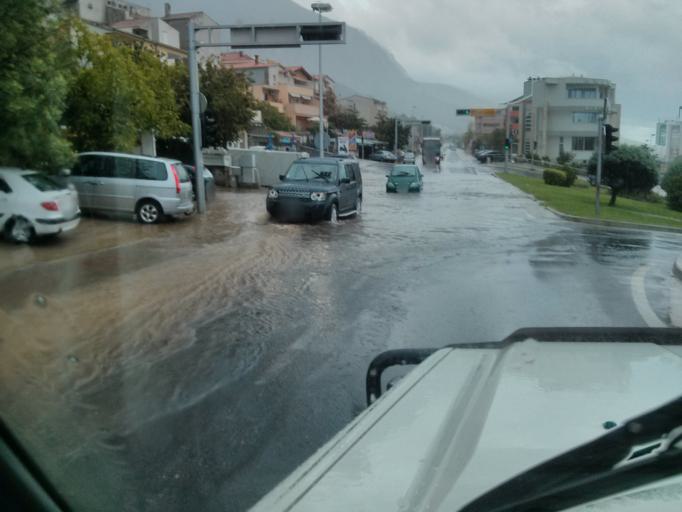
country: HR
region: Splitsko-Dalmatinska
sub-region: Grad Makarska
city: Makarska
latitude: 43.3052
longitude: 17.0094
